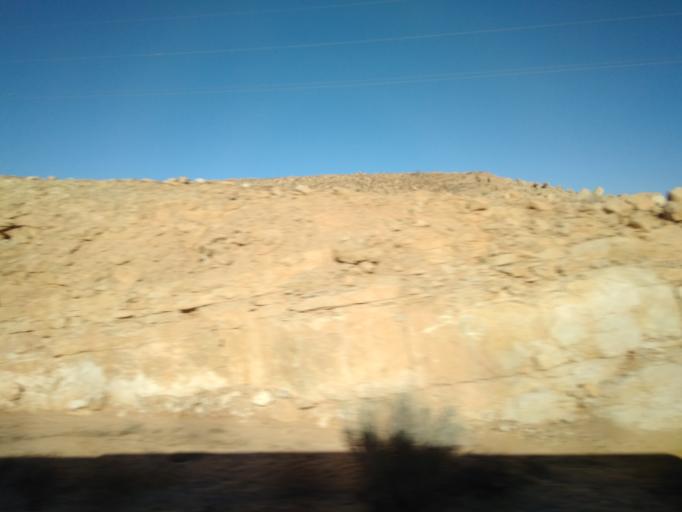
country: IL
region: Southern District
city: Eilat
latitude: 29.6964
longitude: 34.8573
